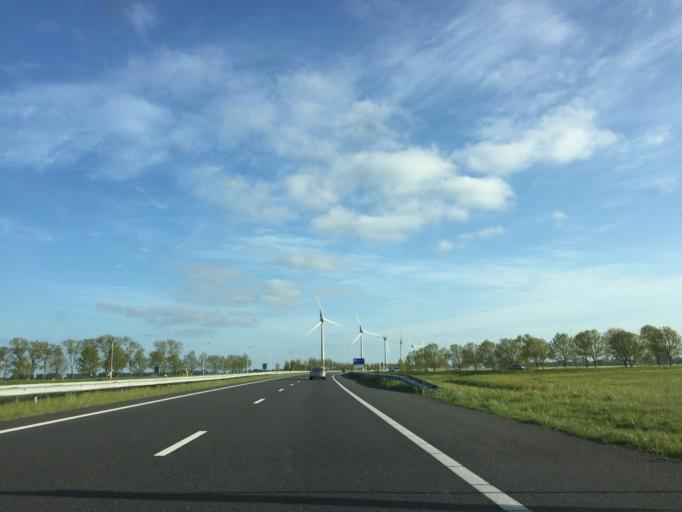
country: NL
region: North Holland
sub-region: Gemeente Medemblik
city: Opperdoes
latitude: 52.7506
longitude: 5.0336
